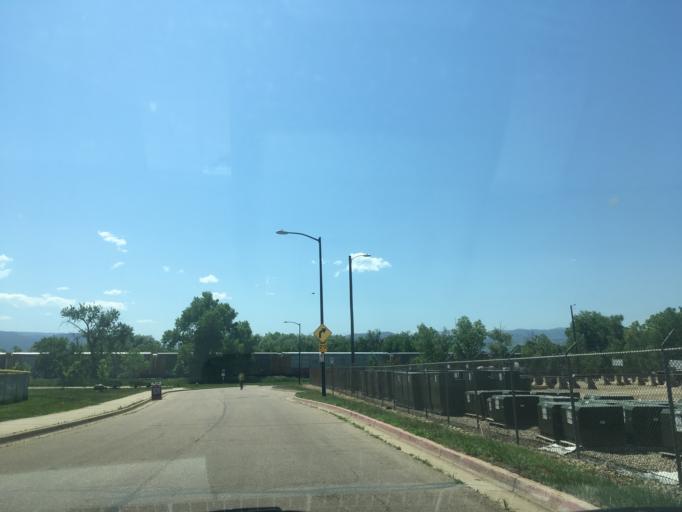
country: US
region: Colorado
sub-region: Boulder County
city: Boulder
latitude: 40.0239
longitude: -105.2136
